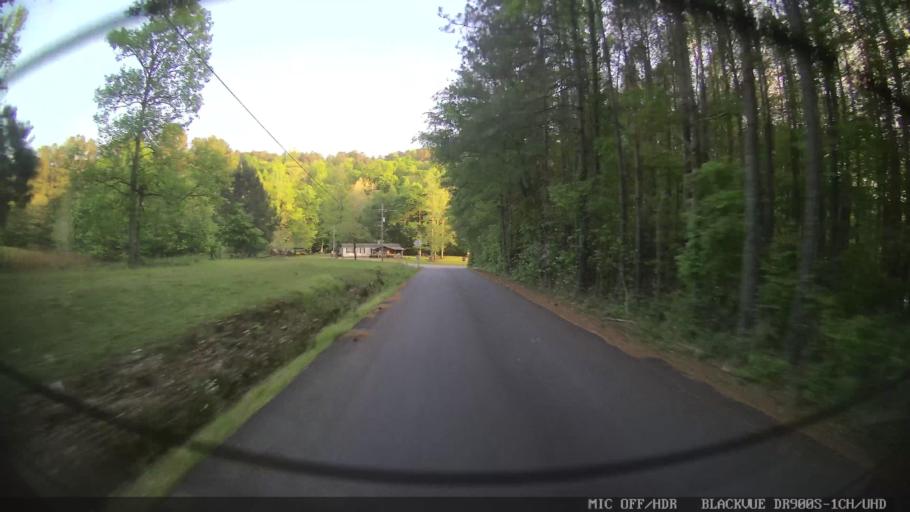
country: US
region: Georgia
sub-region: Bartow County
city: Emerson
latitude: 34.0788
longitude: -84.7712
